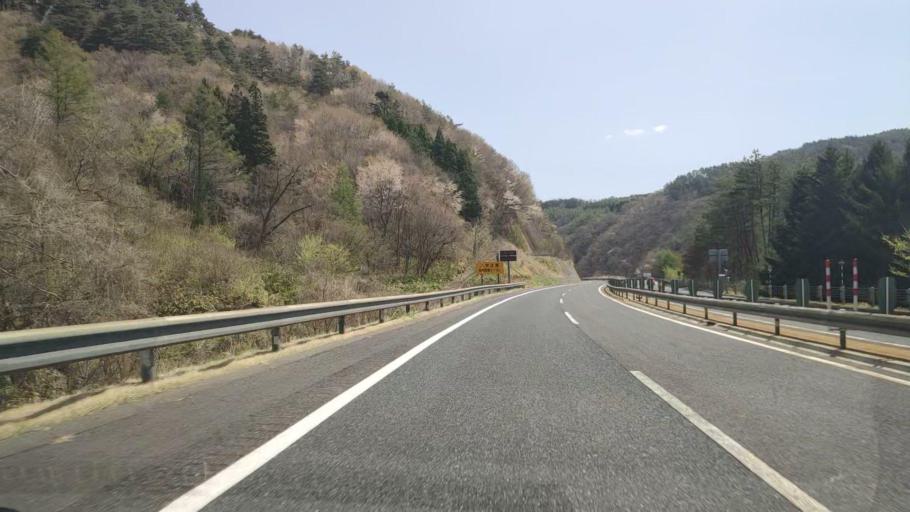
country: JP
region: Iwate
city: Ichinohe
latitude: 40.2227
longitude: 141.2541
